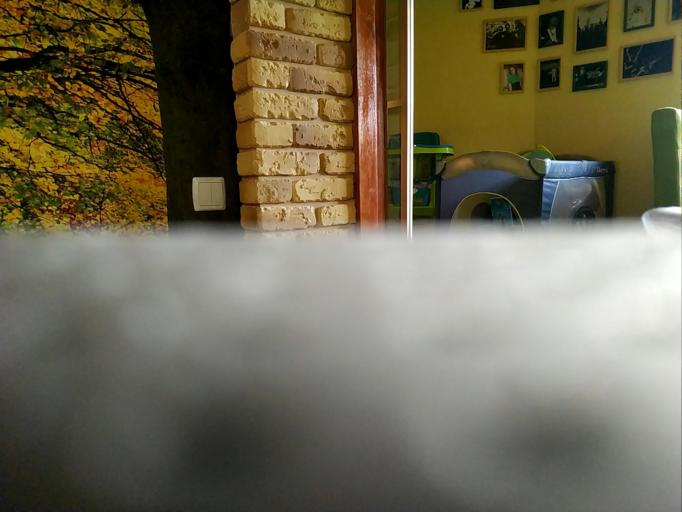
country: RU
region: Kaluga
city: Seredeyskiy
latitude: 54.0430
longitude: 35.3011
